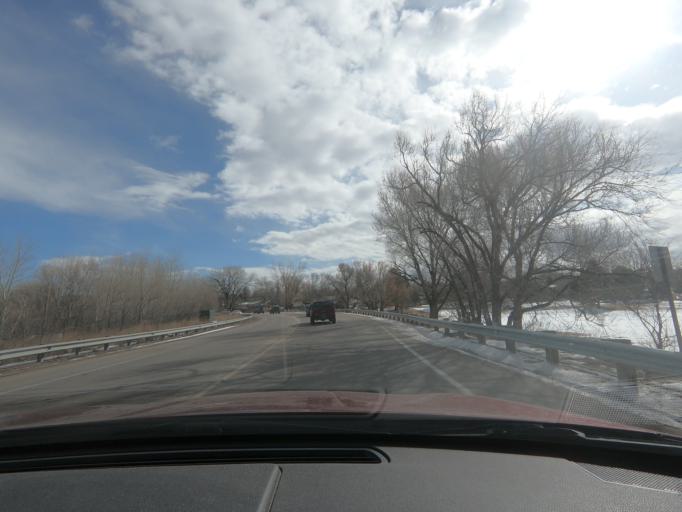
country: US
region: Colorado
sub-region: El Paso County
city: Security-Widefield
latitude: 38.7369
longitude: -104.7108
